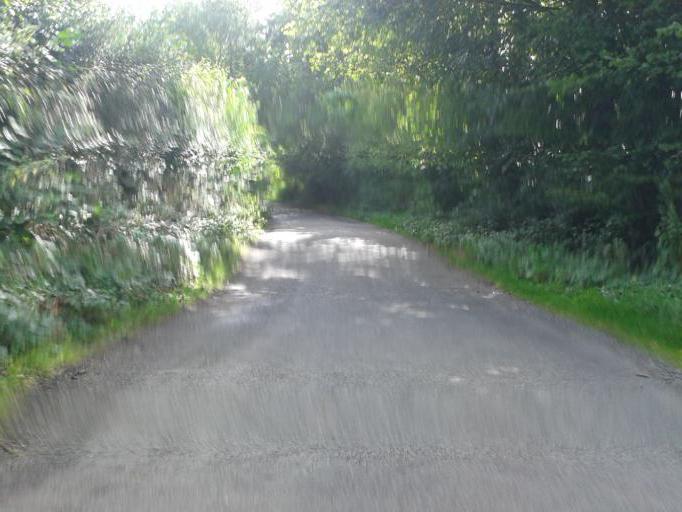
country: GB
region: England
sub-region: Hertfordshire
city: Buntingford
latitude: 51.9754
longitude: 0.0918
